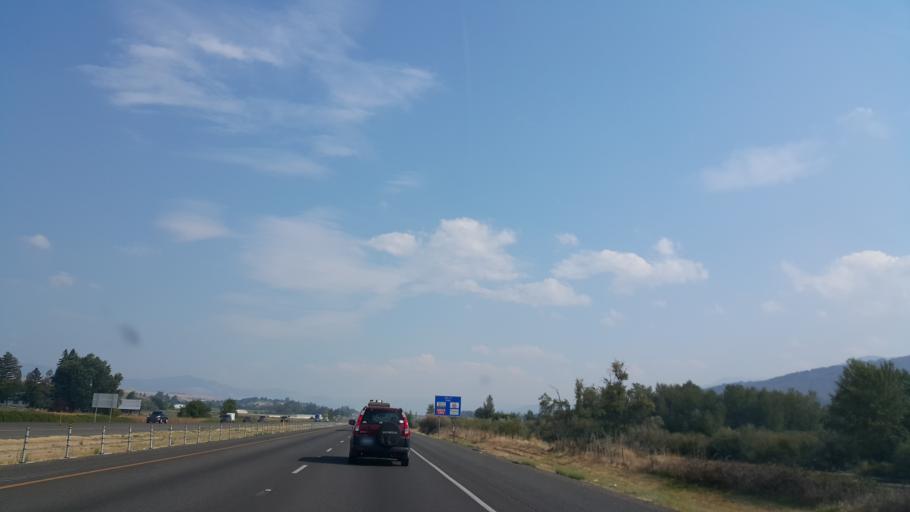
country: US
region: Oregon
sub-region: Jackson County
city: Talent
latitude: 42.2414
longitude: -122.7678
